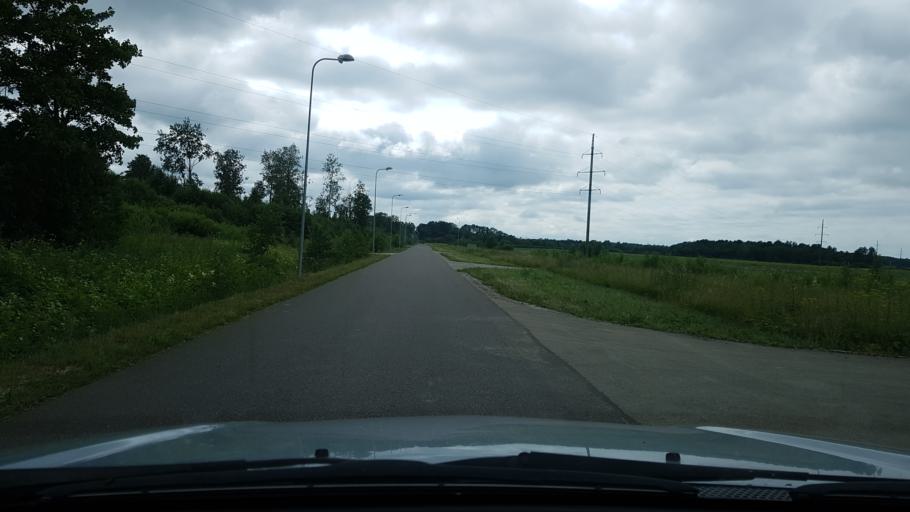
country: EE
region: Ida-Virumaa
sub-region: Narva linn
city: Narva
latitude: 59.3949
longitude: 28.1190
